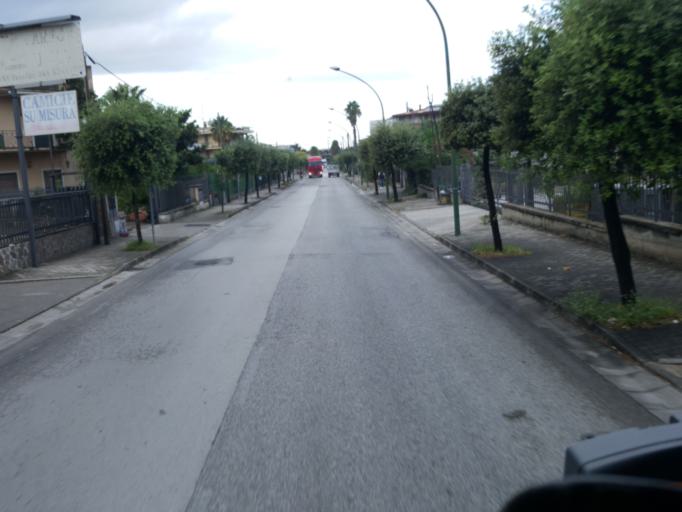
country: IT
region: Campania
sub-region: Provincia di Napoli
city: Palma Campania
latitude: 40.8575
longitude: 14.5523
